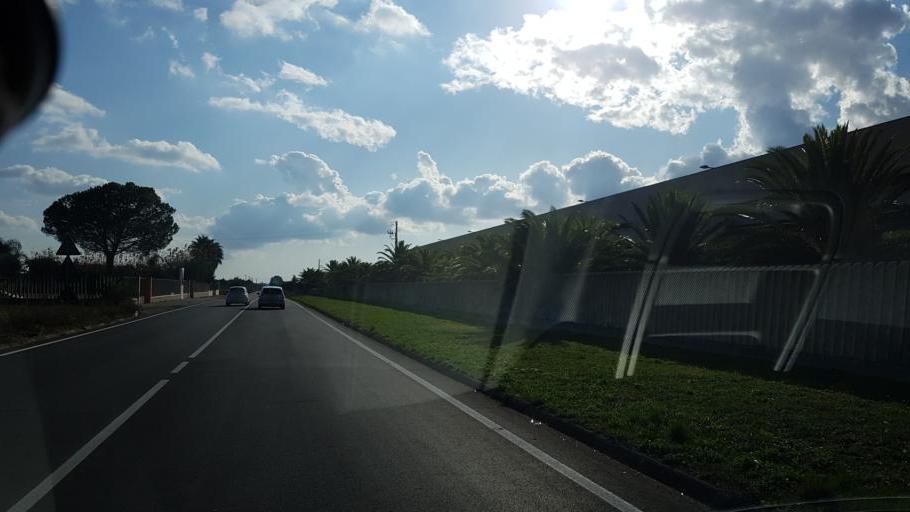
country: IT
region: Apulia
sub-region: Provincia di Lecce
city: Salice Salentino
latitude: 40.3675
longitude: 17.9672
